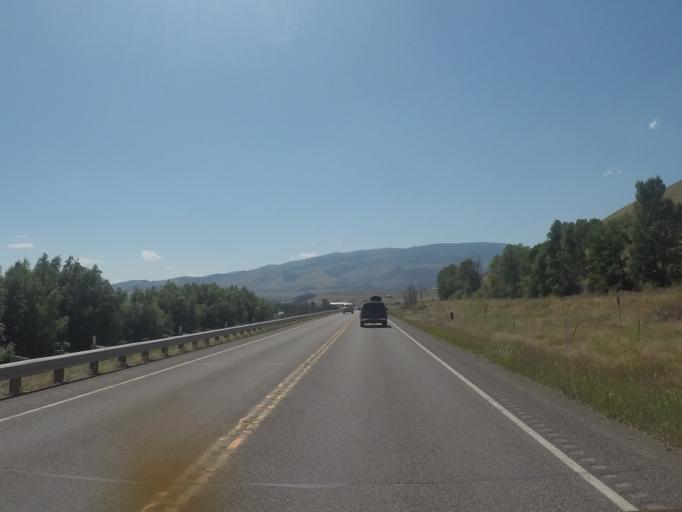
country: US
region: Montana
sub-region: Park County
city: Livingston
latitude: 45.4196
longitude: -110.6693
